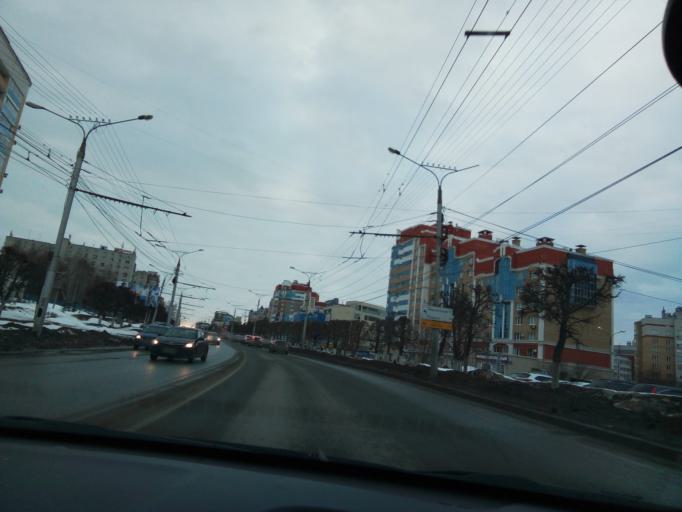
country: RU
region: Chuvashia
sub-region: Cheboksarskiy Rayon
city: Cheboksary
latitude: 56.1487
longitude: 47.1997
